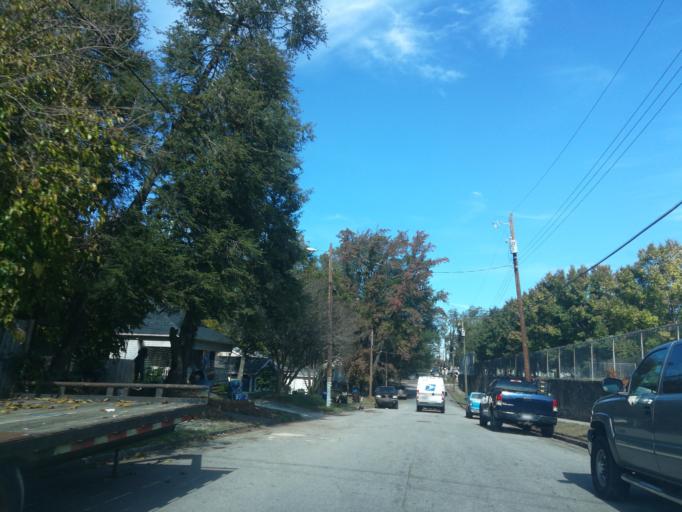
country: US
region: North Carolina
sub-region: Durham County
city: Durham
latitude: 35.9892
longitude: -78.8806
